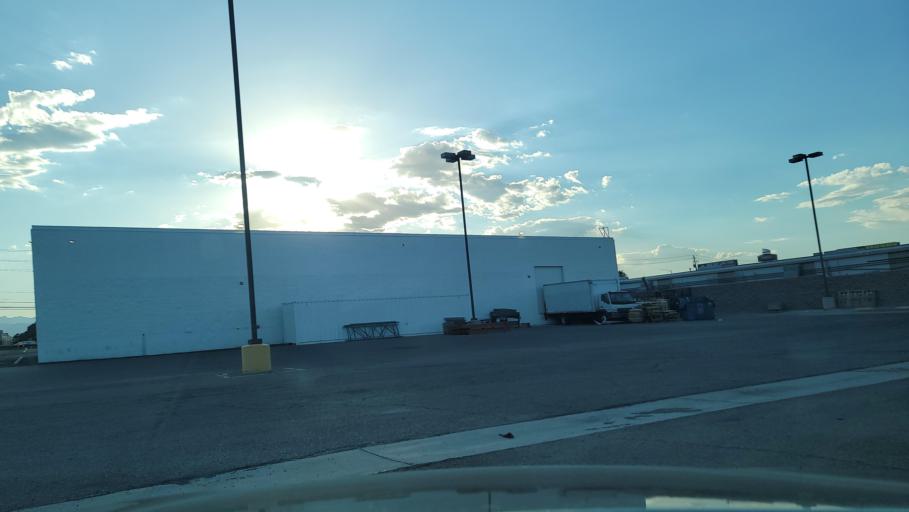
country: US
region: Nevada
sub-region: Clark County
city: Paradise
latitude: 36.1205
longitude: -115.1888
